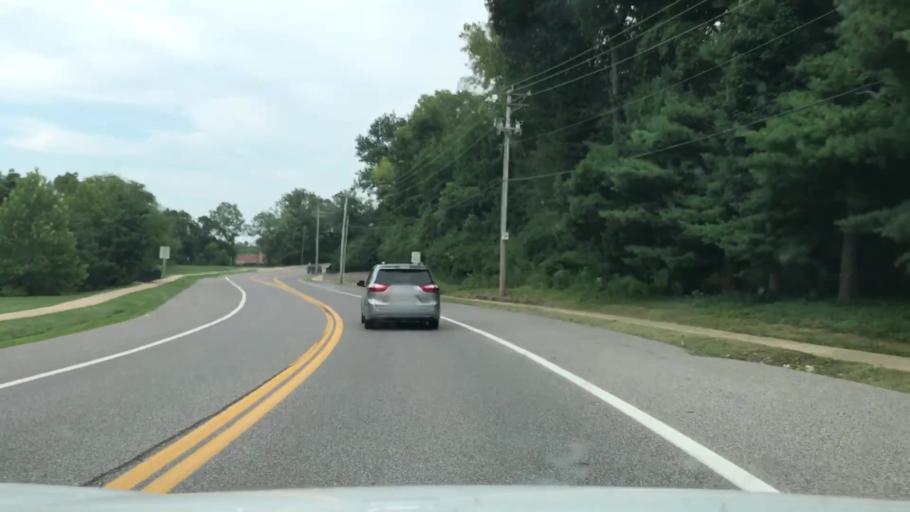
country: US
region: Missouri
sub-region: Saint Louis County
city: Clarkson Valley
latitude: 38.6235
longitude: -90.5883
